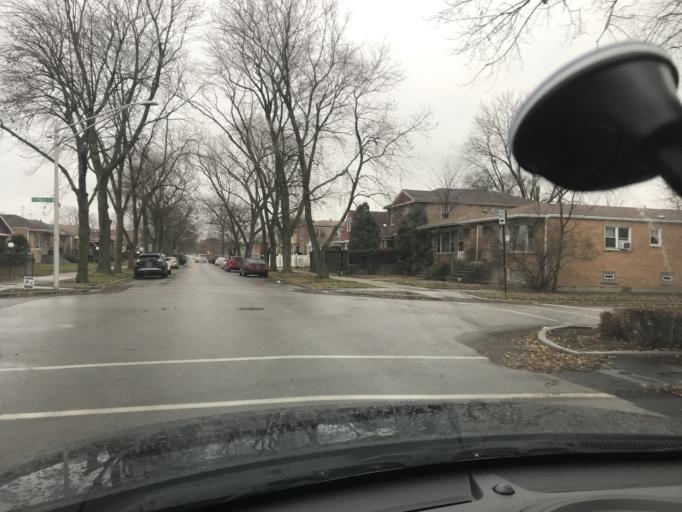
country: US
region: Illinois
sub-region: Cook County
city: Calumet Park
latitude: 41.7199
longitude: -87.6371
